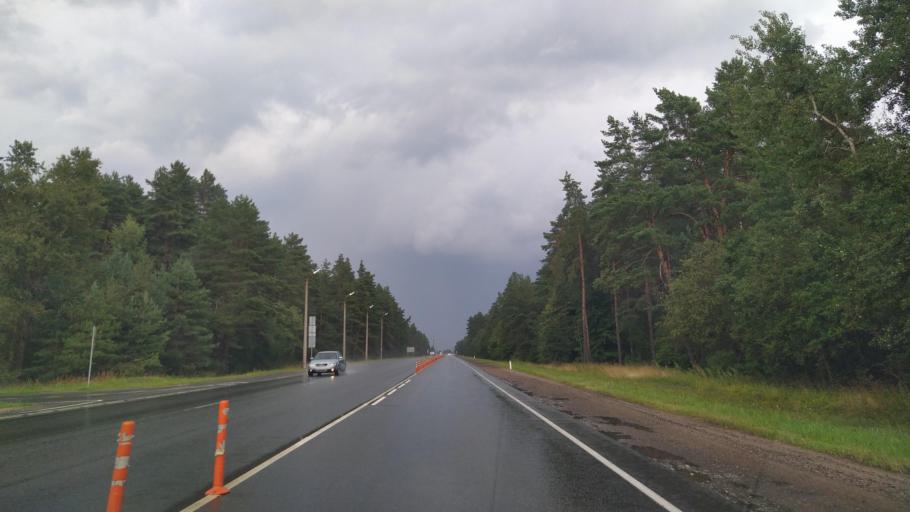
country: RU
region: Pskov
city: Pskov
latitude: 57.7328
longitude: 28.3594
